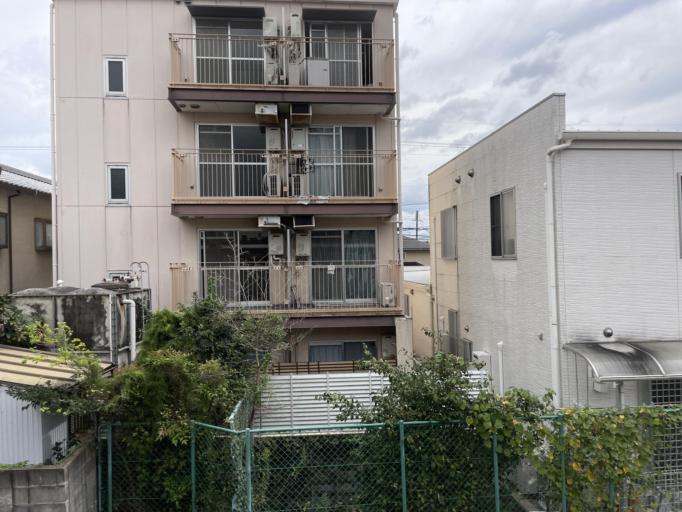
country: JP
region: Hyogo
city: Takarazuka
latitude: 34.8124
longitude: 135.3579
